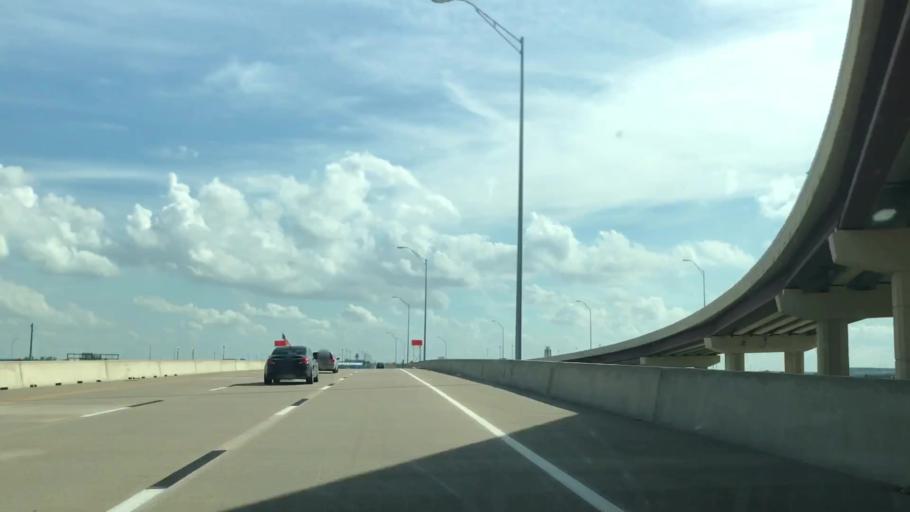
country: US
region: Texas
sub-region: Dallas County
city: Coppell
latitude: 32.9329
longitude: -97.0414
